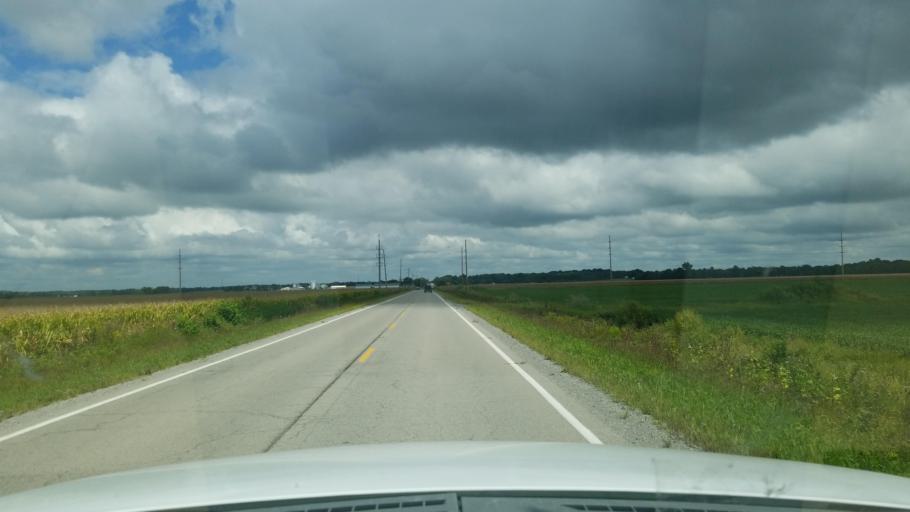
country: US
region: Illinois
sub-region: Saline County
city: Eldorado
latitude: 37.7731
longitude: -88.4381
